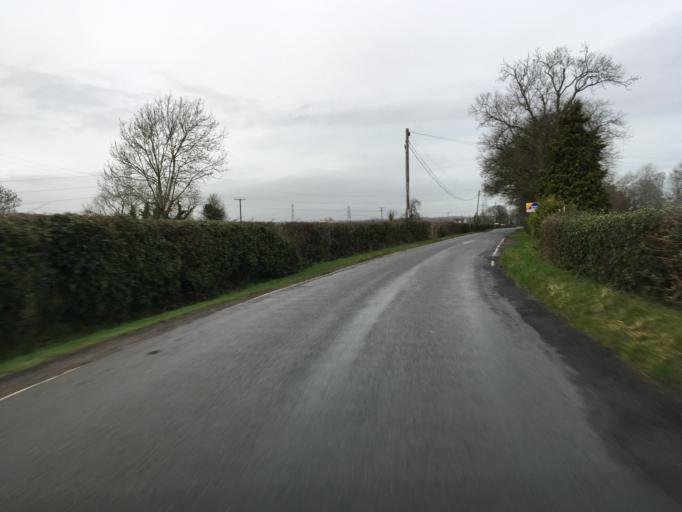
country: GB
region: Wales
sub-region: Newport
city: Goldcliff
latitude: 51.5552
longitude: -2.9093
